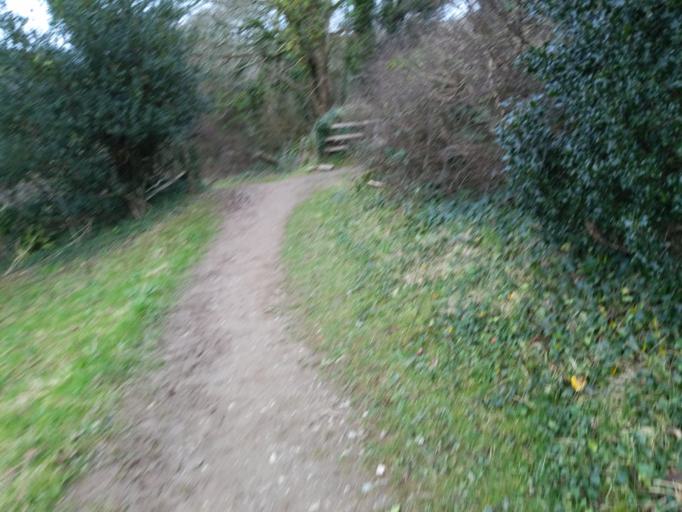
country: GB
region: England
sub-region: Cornwall
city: Fowey
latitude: 50.3360
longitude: -4.6117
